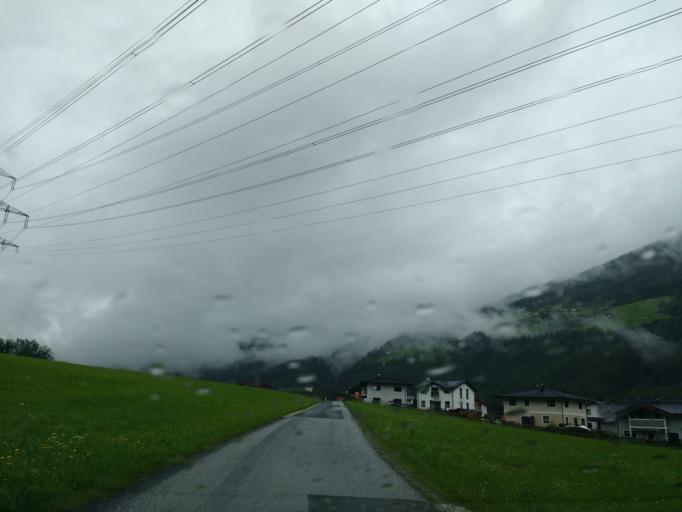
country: AT
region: Salzburg
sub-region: Politischer Bezirk Zell am See
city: Neukirchen am Grossvenediger
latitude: 47.2493
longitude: 12.2932
